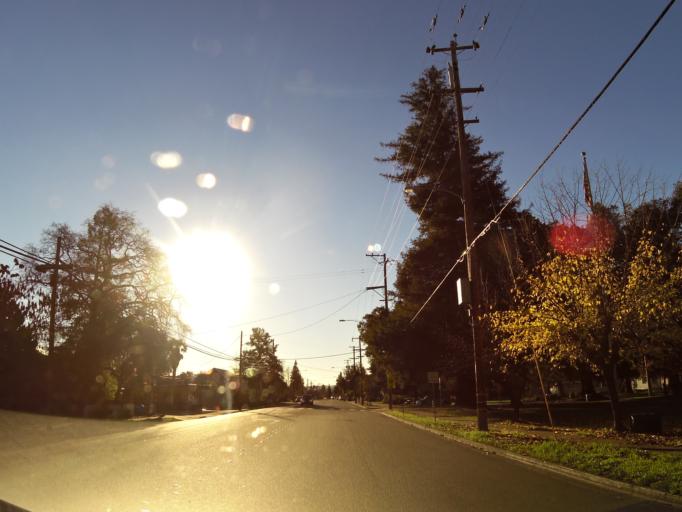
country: US
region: California
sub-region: Sonoma County
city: Cloverdale
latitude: 38.8114
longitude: -123.0216
